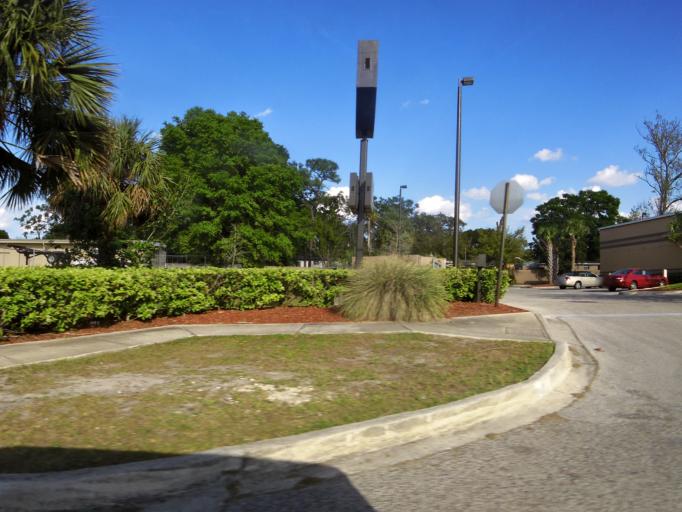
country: US
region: Florida
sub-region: Duval County
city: Jacksonville
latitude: 30.3497
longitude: -81.5966
